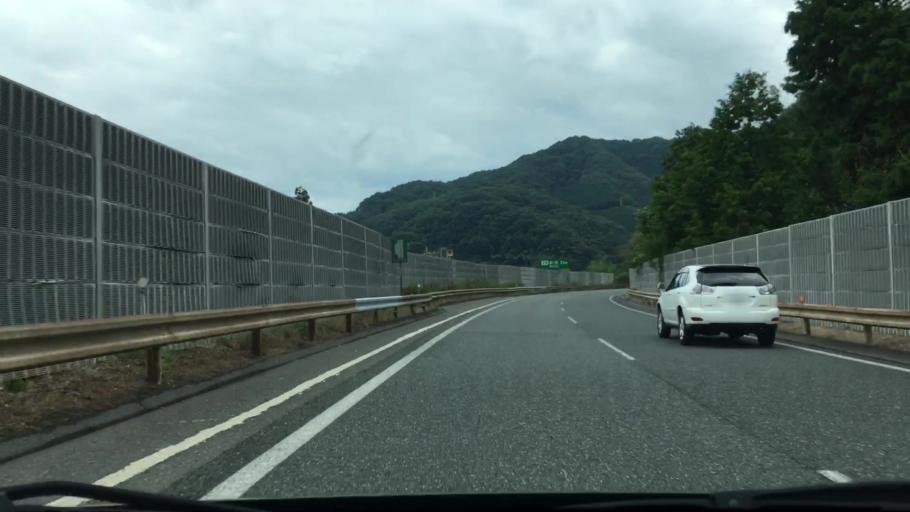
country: JP
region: Okayama
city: Niimi
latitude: 34.9936
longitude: 133.4674
